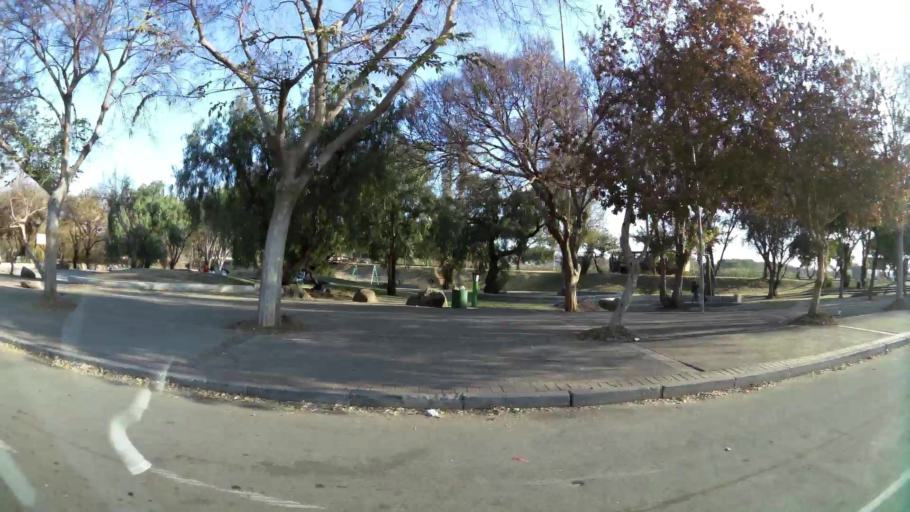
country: ZA
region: Gauteng
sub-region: City of Johannesburg Metropolitan Municipality
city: Soweto
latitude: -26.2614
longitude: 27.8785
